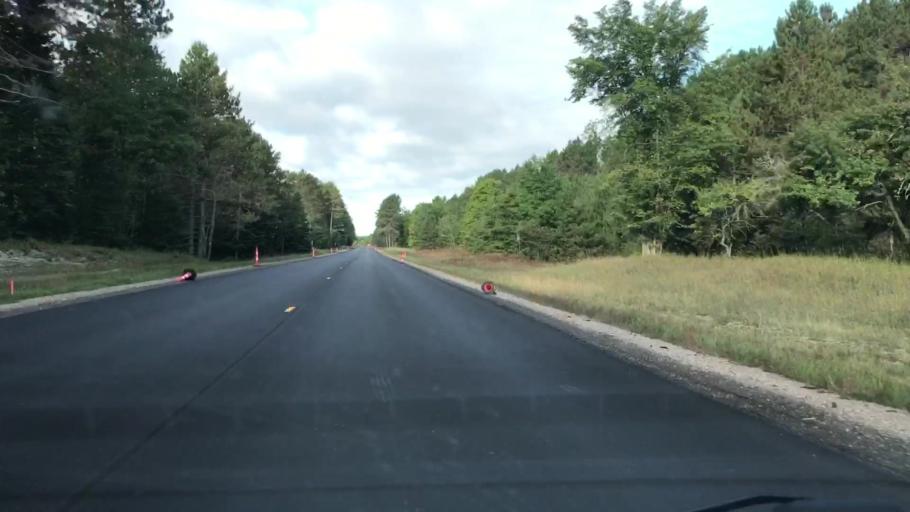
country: US
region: Michigan
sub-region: Luce County
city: Newberry
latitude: 46.3463
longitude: -85.0079
